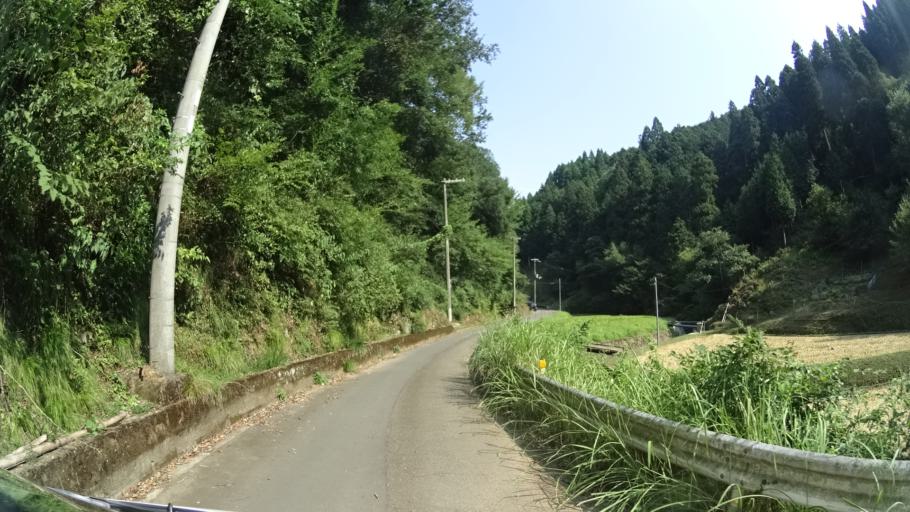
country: JP
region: Kyoto
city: Maizuru
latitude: 35.4070
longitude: 135.2378
